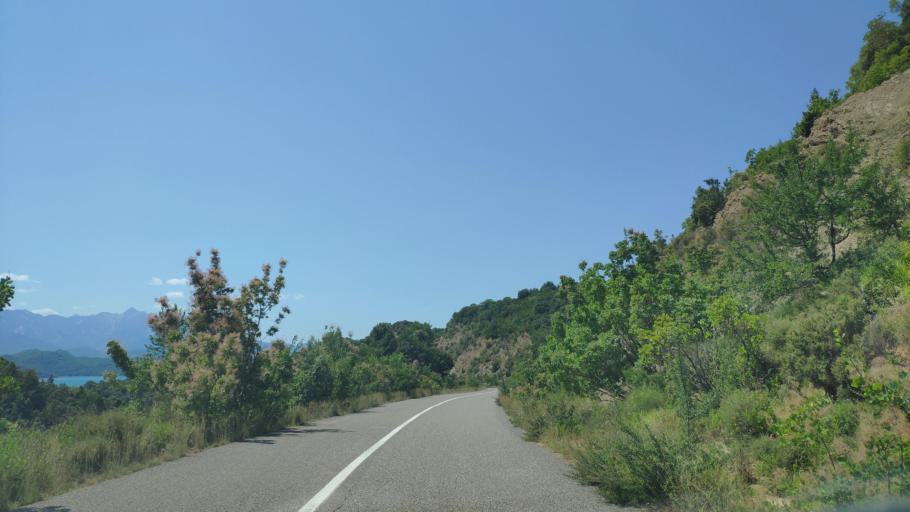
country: GR
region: Central Greece
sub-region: Nomos Evrytanias
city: Kerasochori
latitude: 38.9827
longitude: 21.4933
